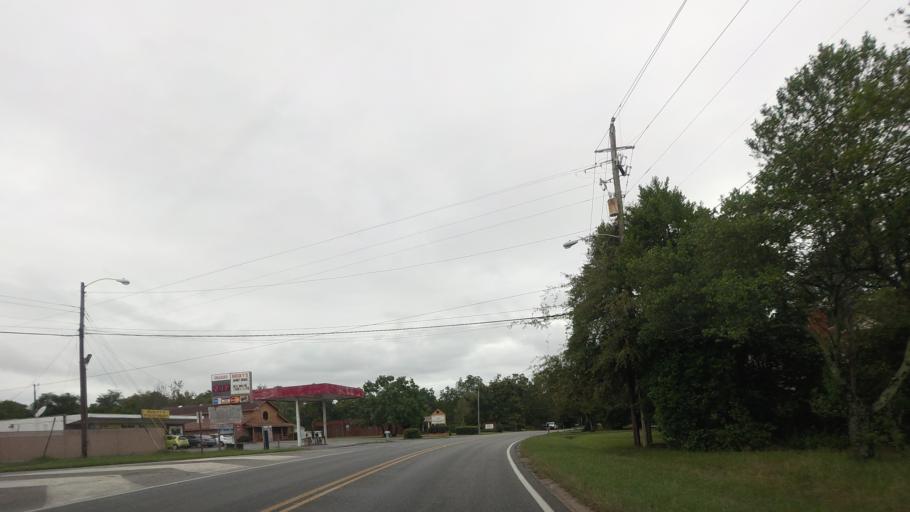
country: US
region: Georgia
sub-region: Houston County
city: Warner Robins
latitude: 32.6087
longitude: -83.6225
